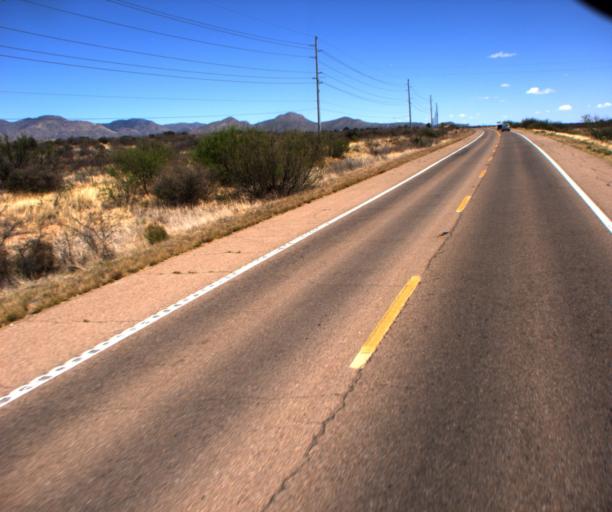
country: US
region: Arizona
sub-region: Cochise County
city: Naco
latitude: 31.3803
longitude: -110.0625
